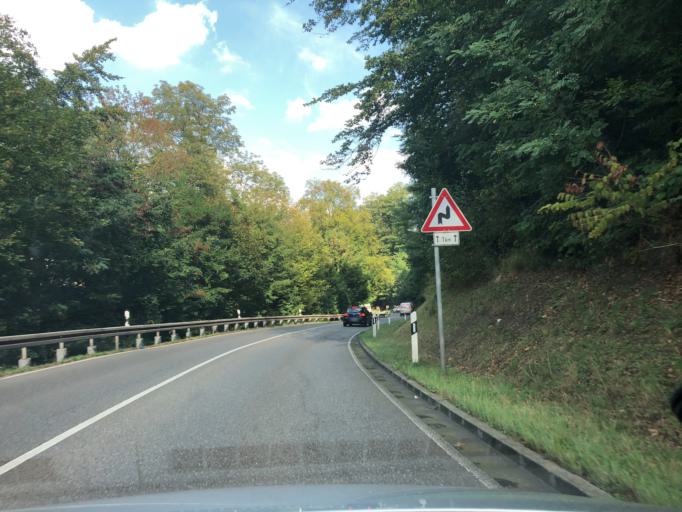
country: DE
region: Baden-Wuerttemberg
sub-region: Regierungsbezirk Stuttgart
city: Stuttgart
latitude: 48.7556
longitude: 9.1525
